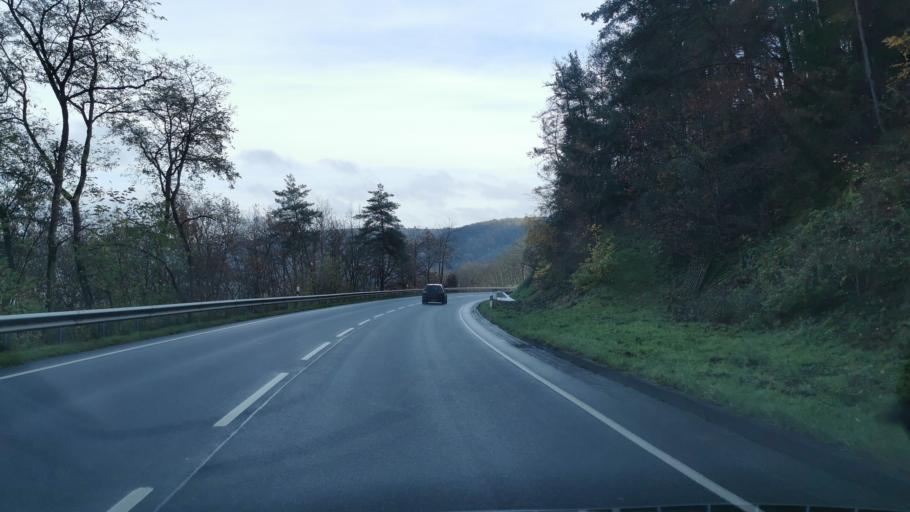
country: DE
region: Rheinland-Pfalz
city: Cochem
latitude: 50.1361
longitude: 7.1712
